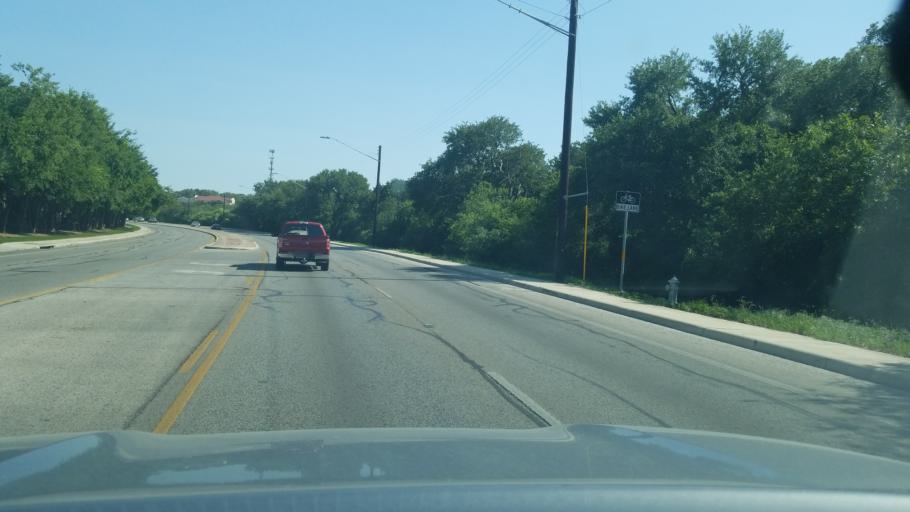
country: US
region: Texas
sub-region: Bexar County
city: Hollywood Park
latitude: 29.5840
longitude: -98.5160
